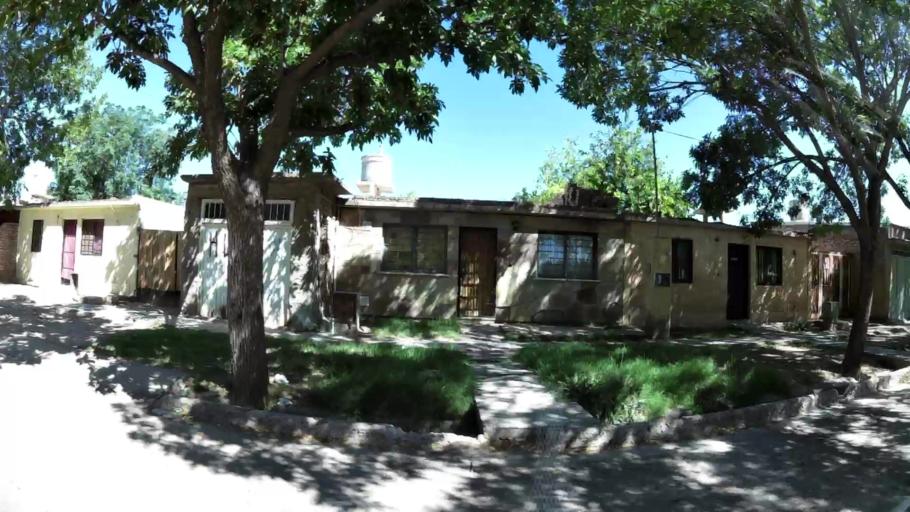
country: AR
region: Mendoza
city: Las Heras
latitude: -32.8282
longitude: -68.8251
